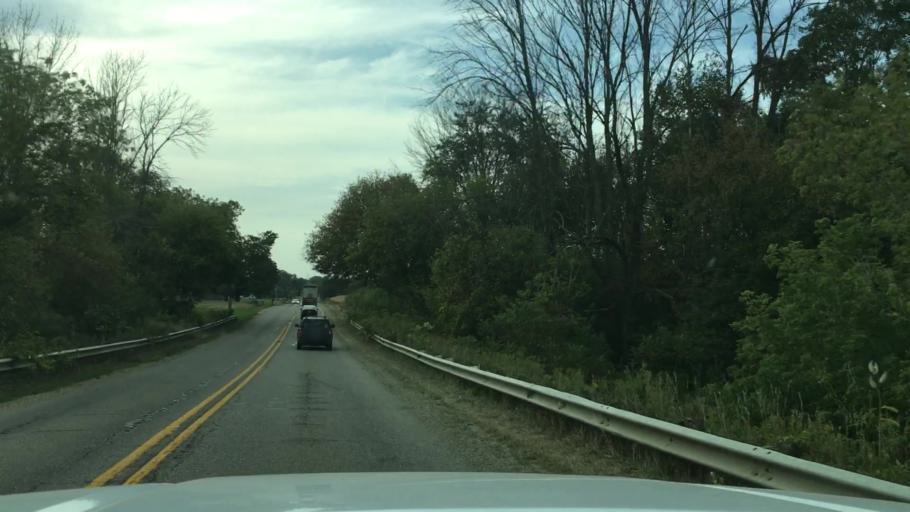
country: US
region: Michigan
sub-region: Ottawa County
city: Hudsonville
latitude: 42.7821
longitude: -85.8556
